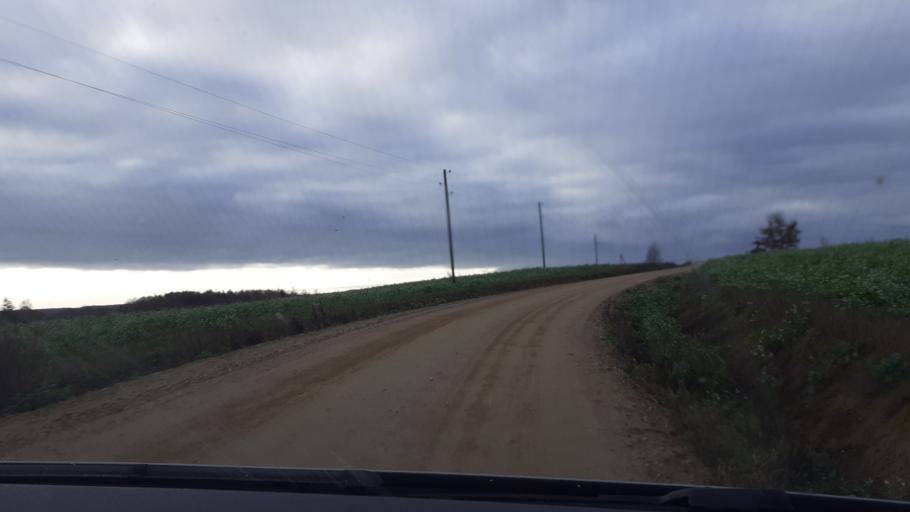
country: LV
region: Aizpute
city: Aizpute
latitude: 56.7704
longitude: 21.8085
